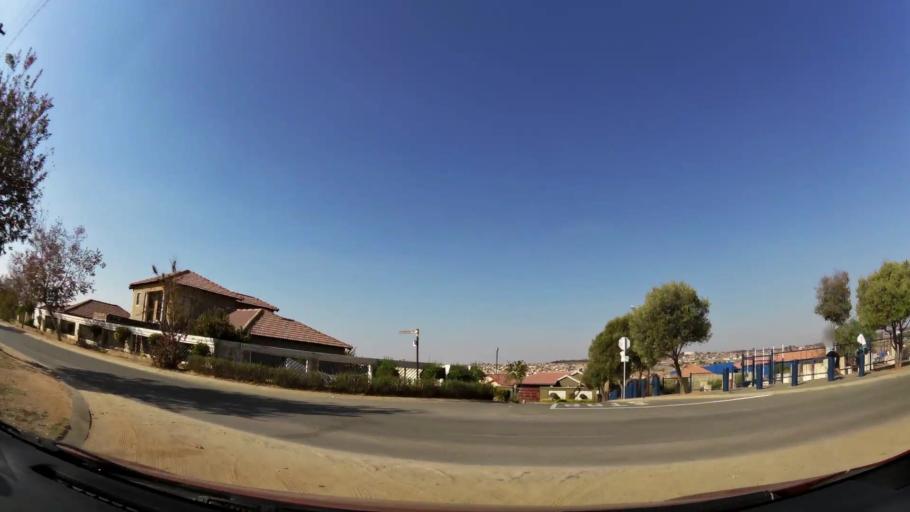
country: ZA
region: Gauteng
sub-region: West Rand District Municipality
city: Muldersdriseloop
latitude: -26.0399
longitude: 27.9123
